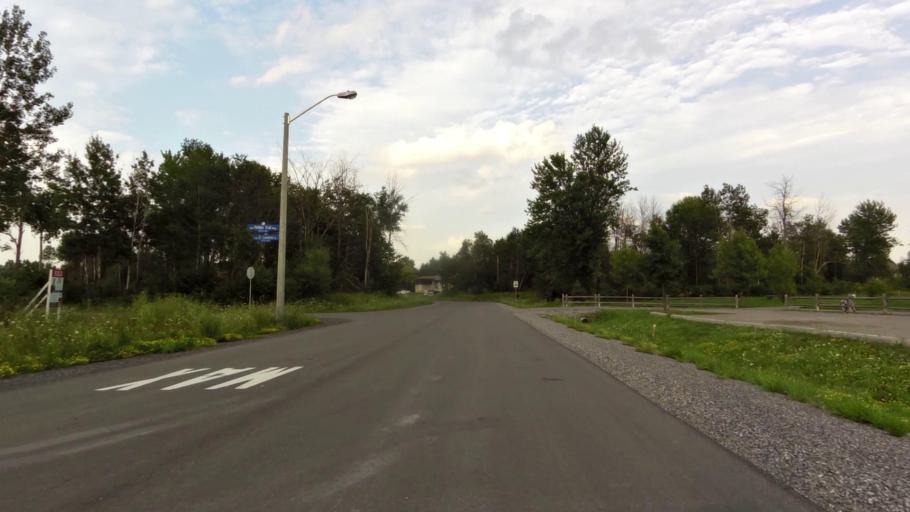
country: CA
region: Ontario
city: Ottawa
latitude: 45.2648
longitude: -75.5839
